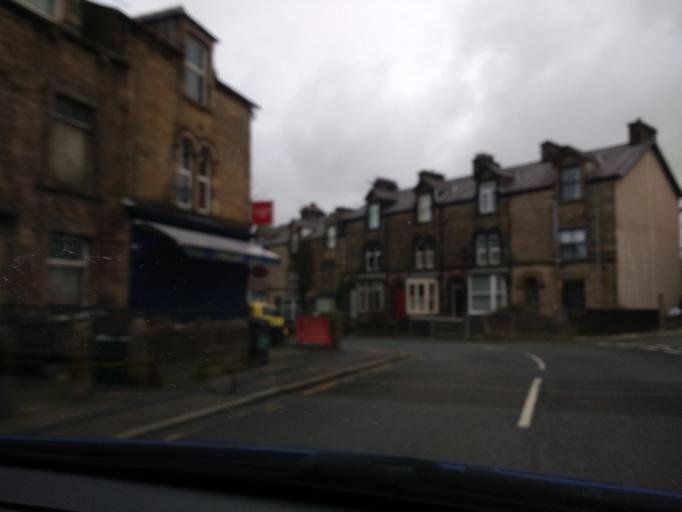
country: GB
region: England
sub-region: Lancashire
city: Lancaster
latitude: 54.0510
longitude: -2.7903
